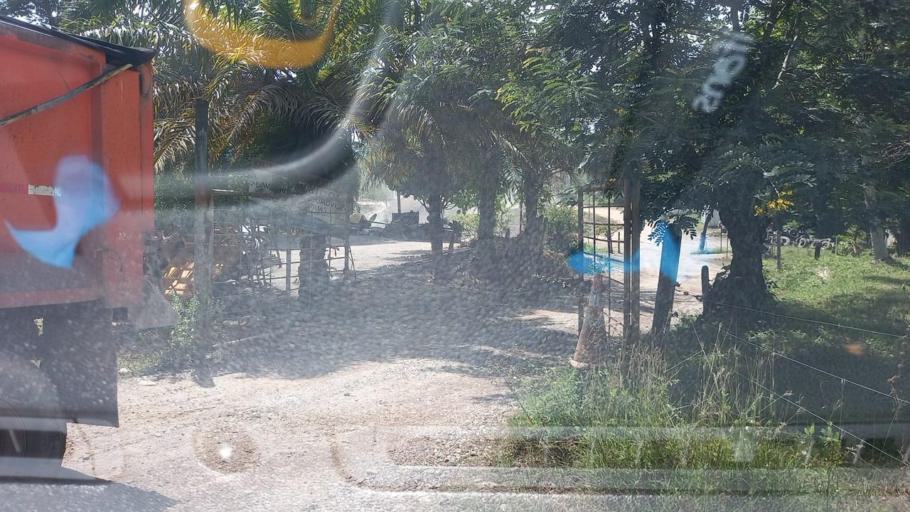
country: CO
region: Santander
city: Barrancabermeja
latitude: 7.1196
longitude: -73.6016
